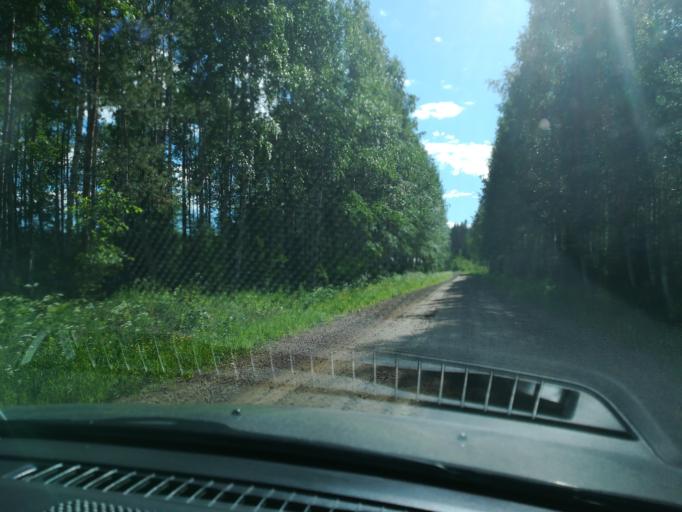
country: FI
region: Southern Savonia
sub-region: Mikkeli
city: Puumala
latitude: 61.6595
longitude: 28.1305
